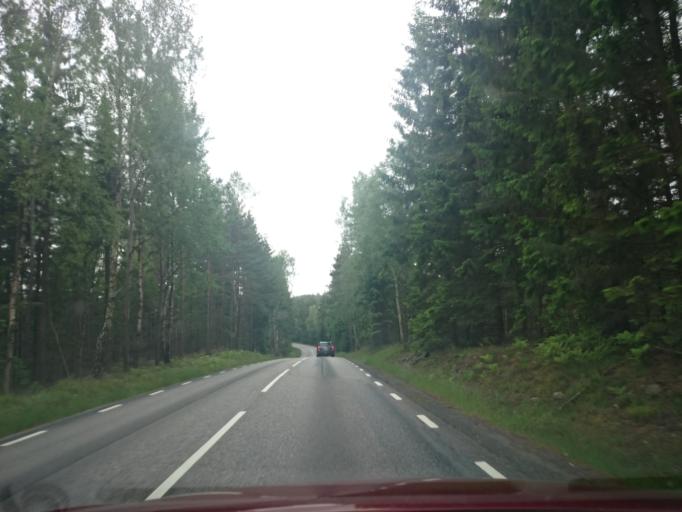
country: SE
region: Vaestra Goetaland
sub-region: Lerums Kommun
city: Stenkullen
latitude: 57.7183
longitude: 12.3455
